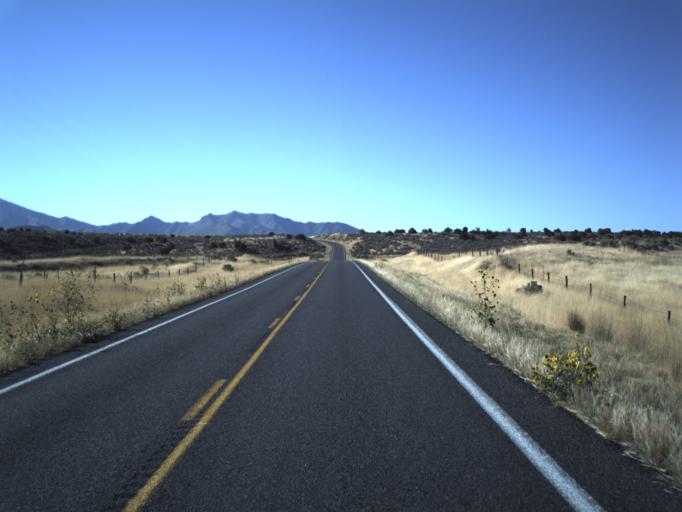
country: US
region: Utah
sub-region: Millard County
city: Delta
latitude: 39.5229
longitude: -112.2734
